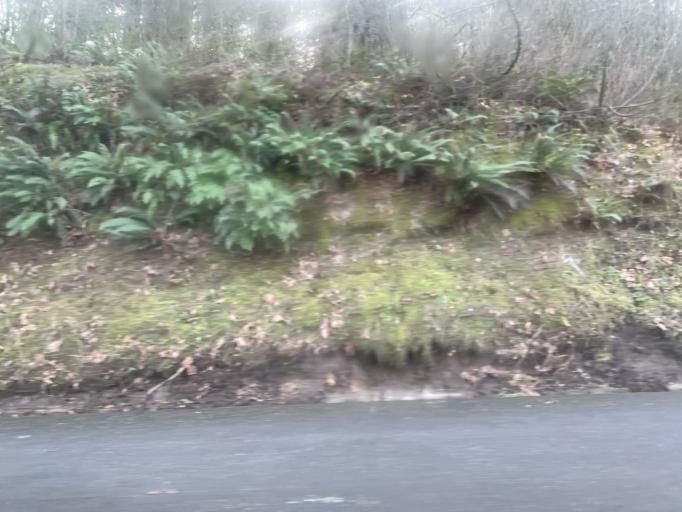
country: US
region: Washington
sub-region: Clark County
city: Washougal
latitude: 45.5358
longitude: -122.2313
